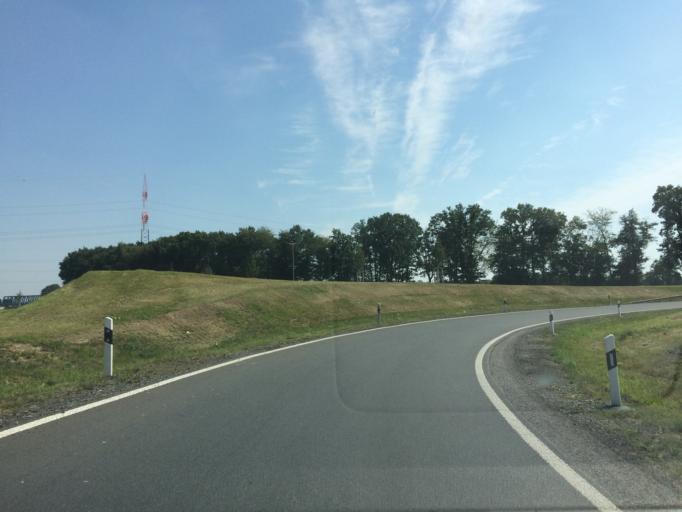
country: DE
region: North Rhine-Westphalia
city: Kamen
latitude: 51.6007
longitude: 7.6889
